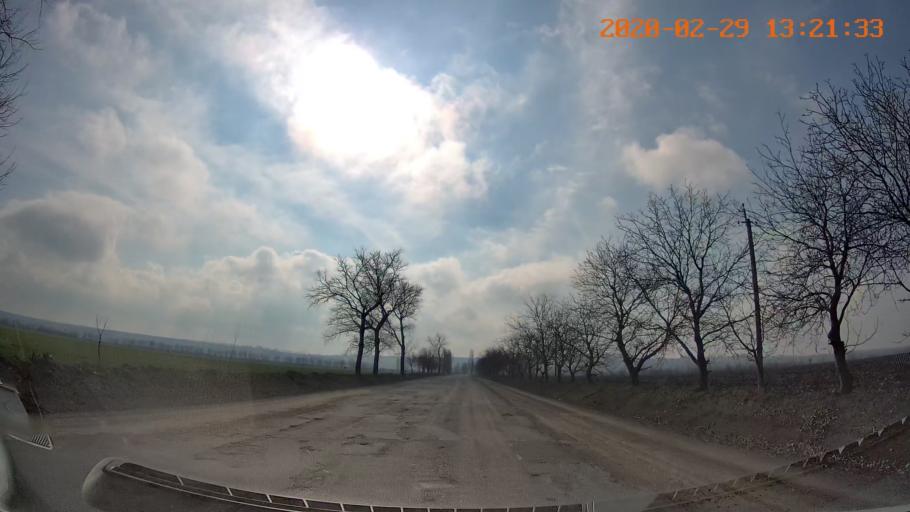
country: MD
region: Telenesti
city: Camenca
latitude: 47.9692
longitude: 28.6319
